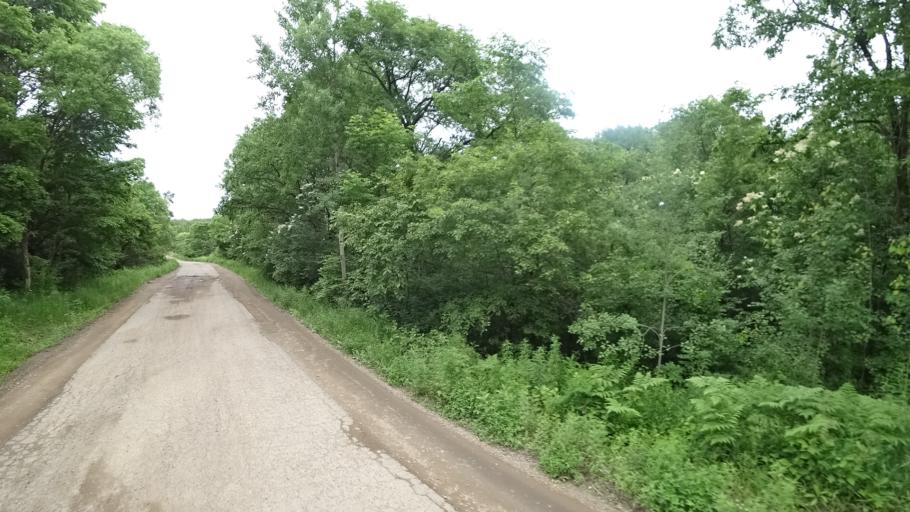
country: RU
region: Primorskiy
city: Novosysoyevka
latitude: 44.2033
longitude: 133.3231
